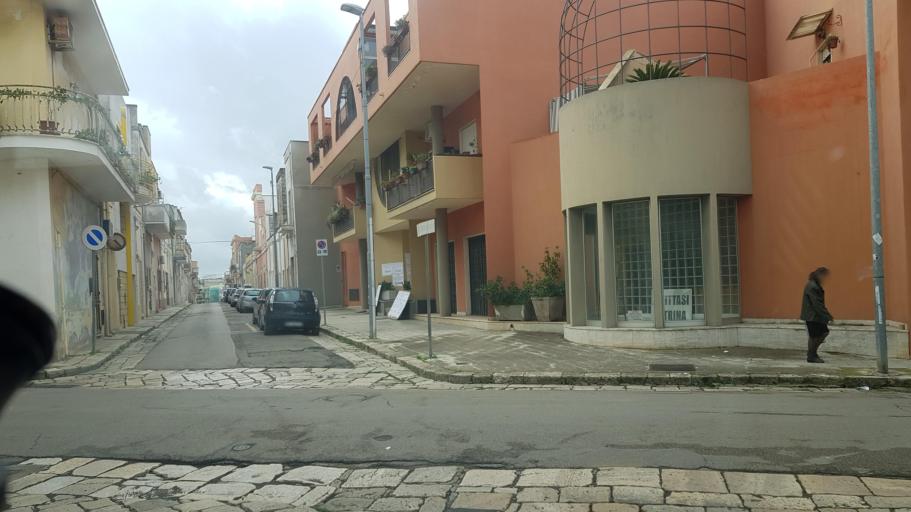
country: IT
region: Apulia
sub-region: Provincia di Lecce
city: Novoli
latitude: 40.3773
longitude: 18.0465
